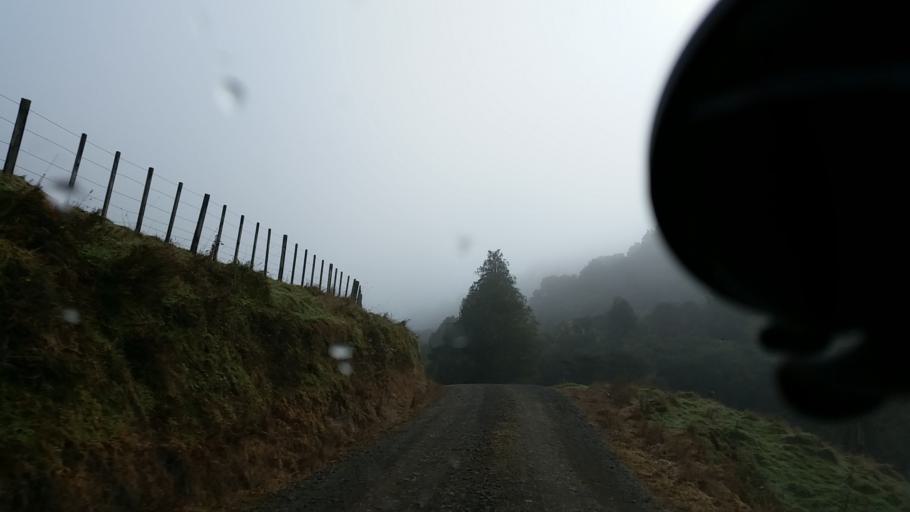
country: NZ
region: Taranaki
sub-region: New Plymouth District
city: Waitara
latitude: -38.9698
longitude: 174.7976
